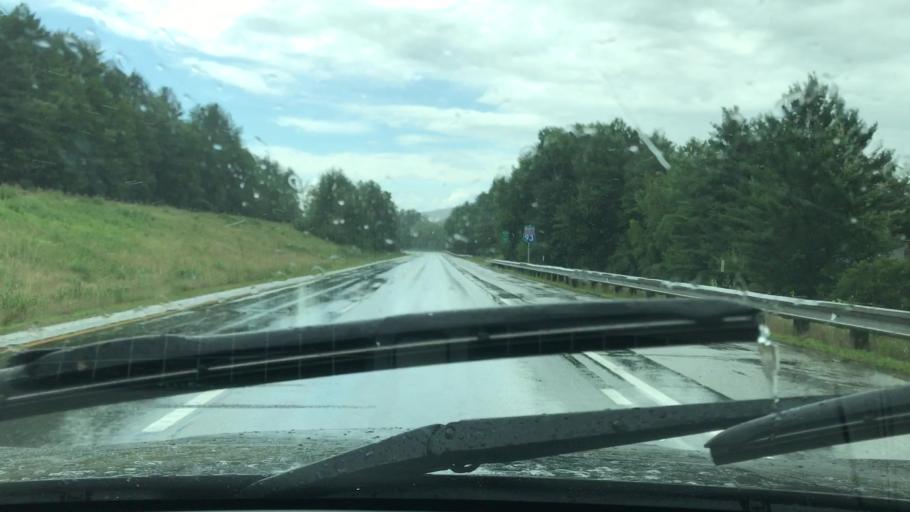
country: US
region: New Hampshire
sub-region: Grafton County
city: Littleton
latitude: 44.2992
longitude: -71.7732
